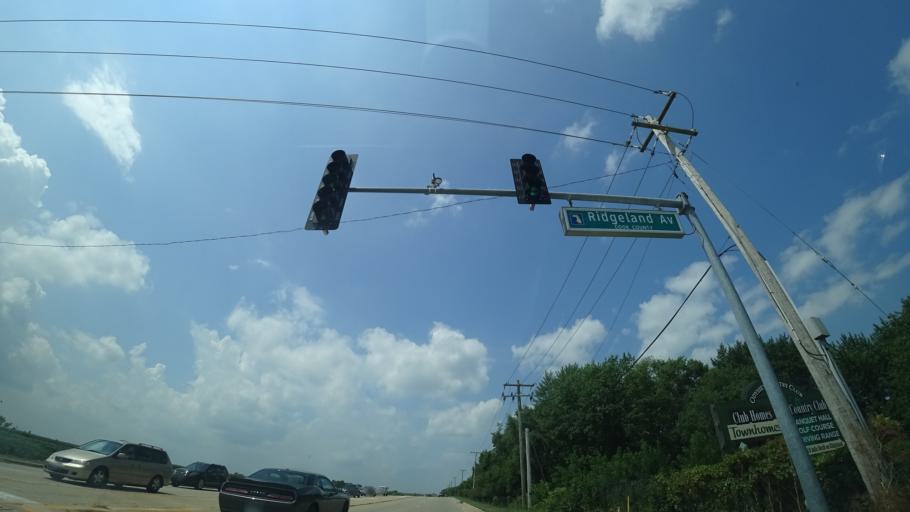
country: US
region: Illinois
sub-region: Will County
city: Frankfort Square
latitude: 41.5271
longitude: -87.7715
